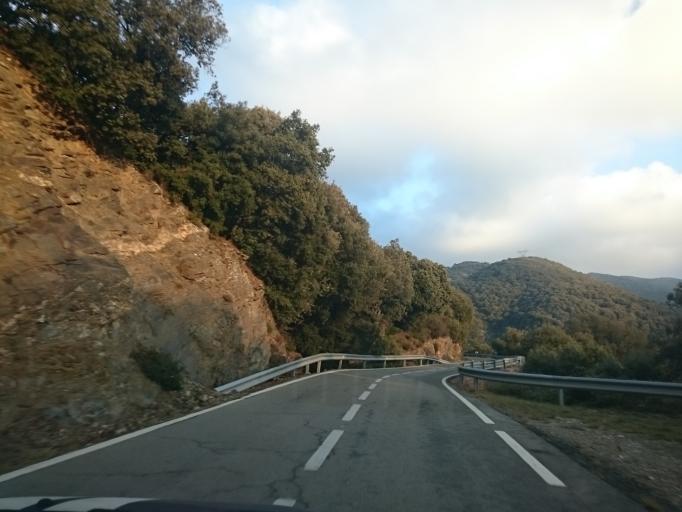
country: ES
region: Catalonia
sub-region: Provincia de Barcelona
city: Seva
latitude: 41.8172
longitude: 2.3246
